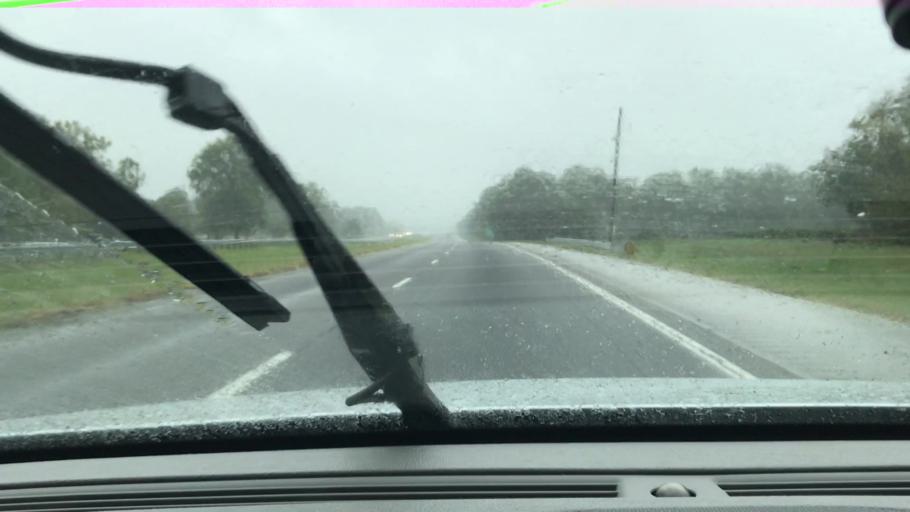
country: US
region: Alabama
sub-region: Limestone County
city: Ardmore
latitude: 34.9538
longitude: -86.8914
